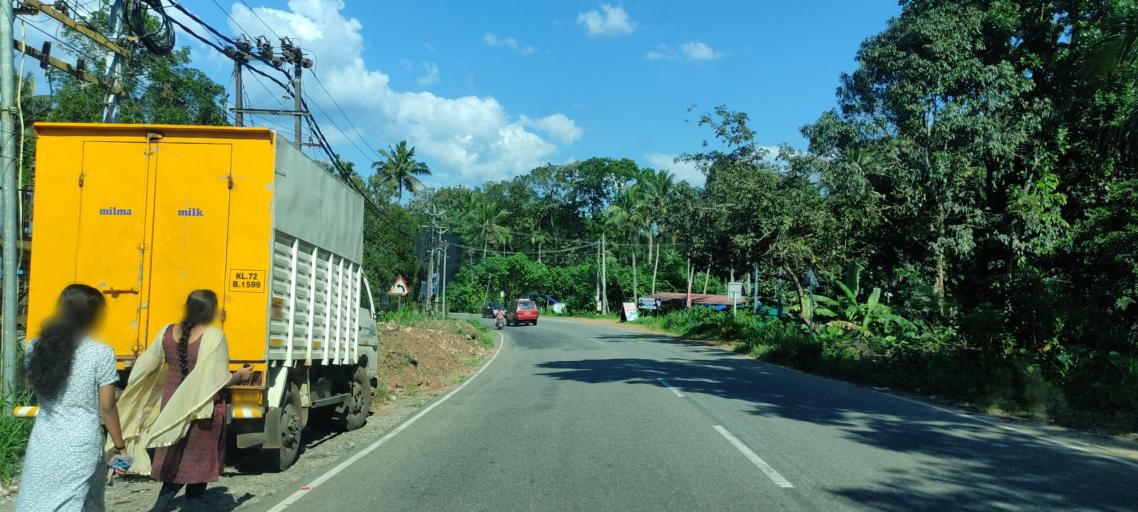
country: IN
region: Kerala
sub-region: Pattanamtitta
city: Pathanamthitta
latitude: 9.2321
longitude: 76.7542
